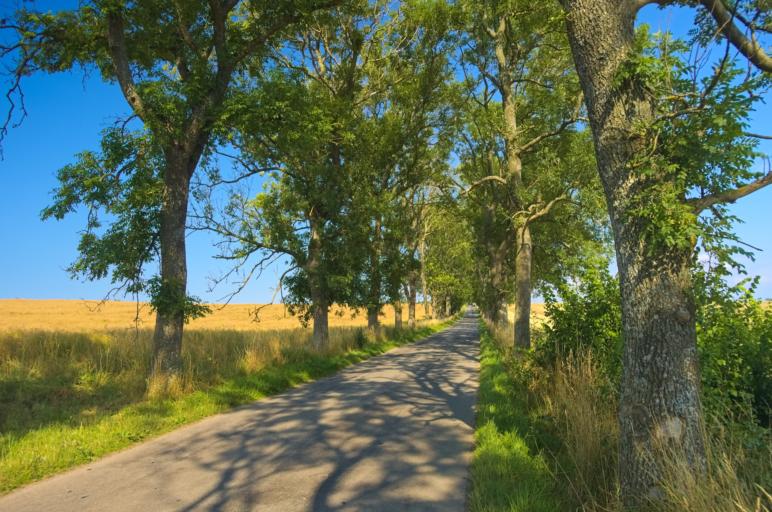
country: PL
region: Pomeranian Voivodeship
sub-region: Powiat slupski
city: Ustka
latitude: 54.5213
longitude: 16.7437
